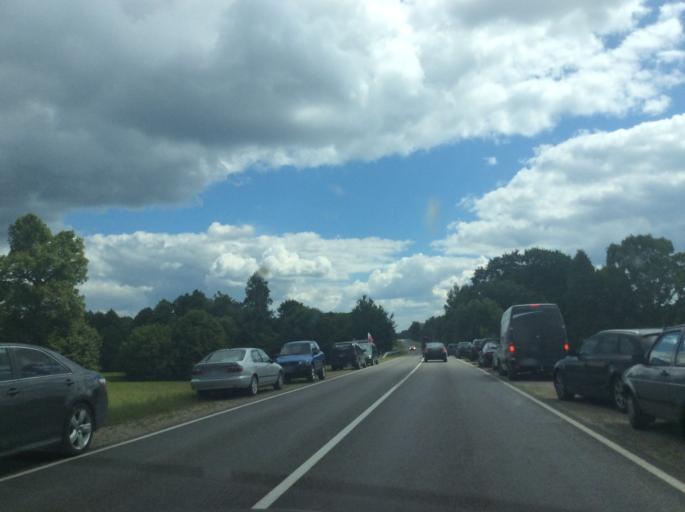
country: LT
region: Alytaus apskritis
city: Druskininkai
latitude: 54.0600
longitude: 23.9224
